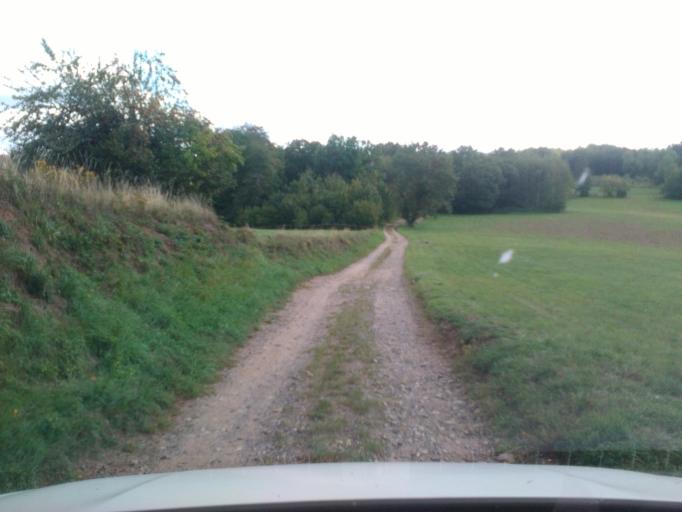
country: FR
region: Lorraine
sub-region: Departement des Vosges
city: Senones
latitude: 48.3890
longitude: 7.0130
